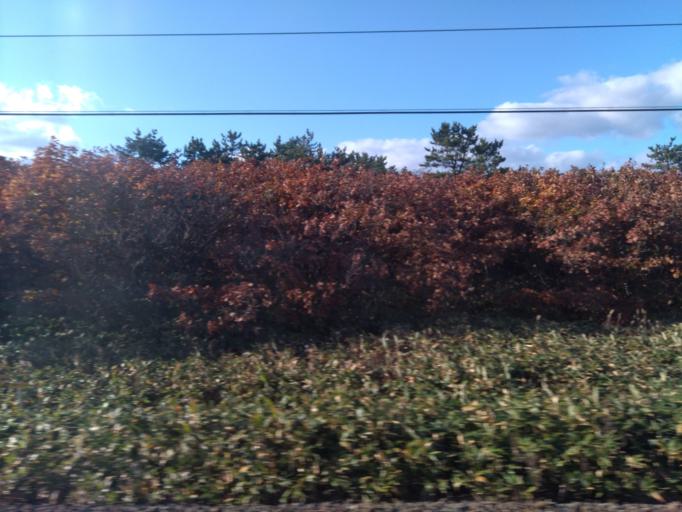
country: JP
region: Hokkaido
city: Niseko Town
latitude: 42.5572
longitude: 140.4257
